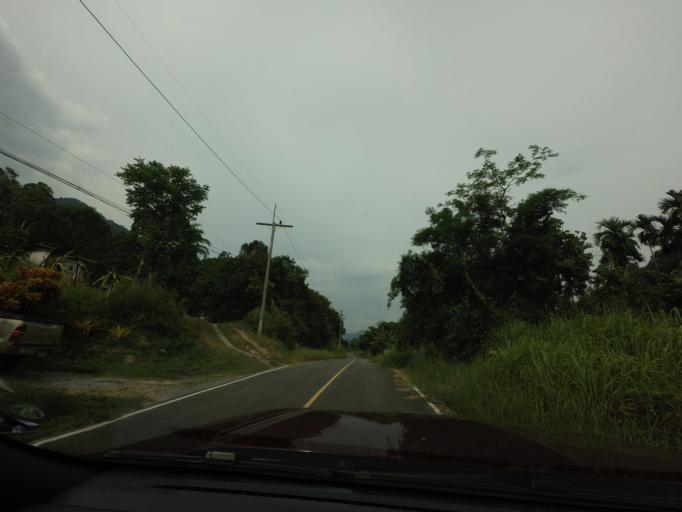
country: TH
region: Narathiwat
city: Si Sakhon
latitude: 6.0608
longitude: 101.3941
